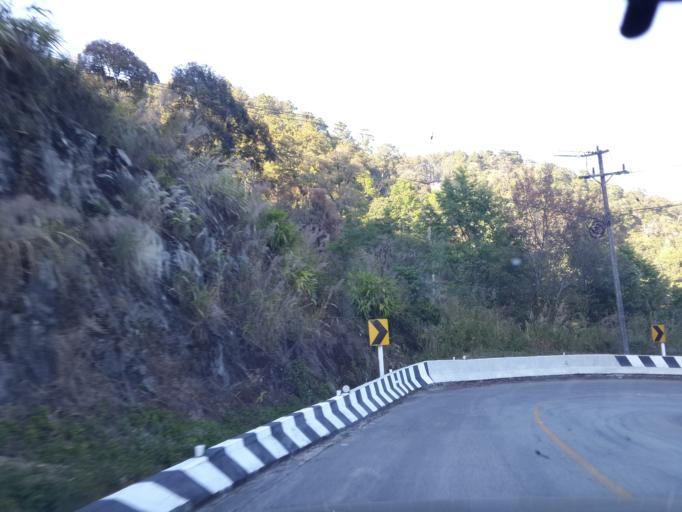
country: TH
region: Chiang Mai
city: Chai Prakan
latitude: 19.8593
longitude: 99.0500
